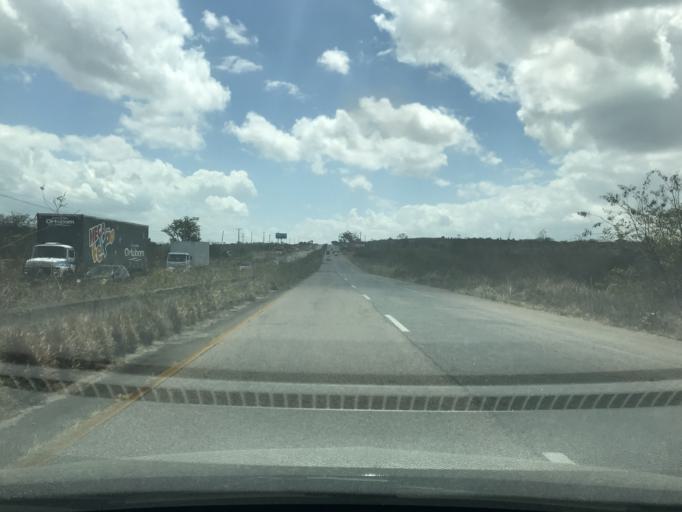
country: BR
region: Pernambuco
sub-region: Caruaru
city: Caruaru
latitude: -8.3025
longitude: -35.9204
